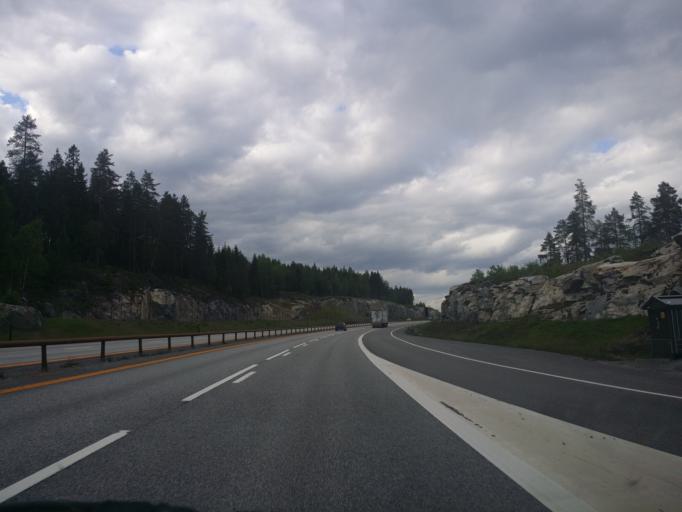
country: NO
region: Akershus
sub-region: Eidsvoll
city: Raholt
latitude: 60.2898
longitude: 11.1336
